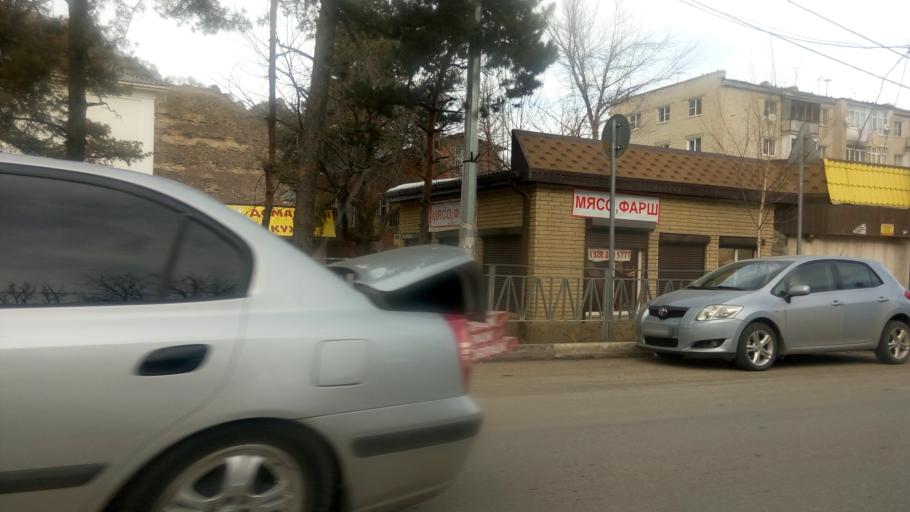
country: RU
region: Karachayevo-Cherkesiya
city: Karachayevsk
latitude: 43.7704
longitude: 41.9090
